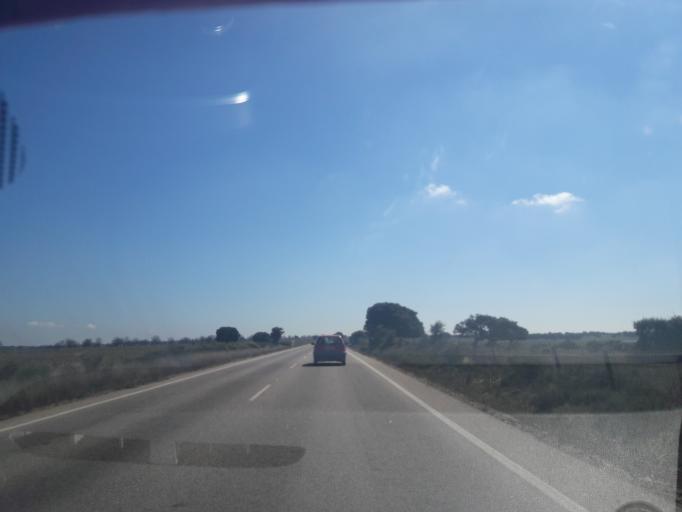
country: ES
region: Castille and Leon
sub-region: Provincia de Salamanca
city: Villasdardo
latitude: 41.0319
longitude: -6.1664
